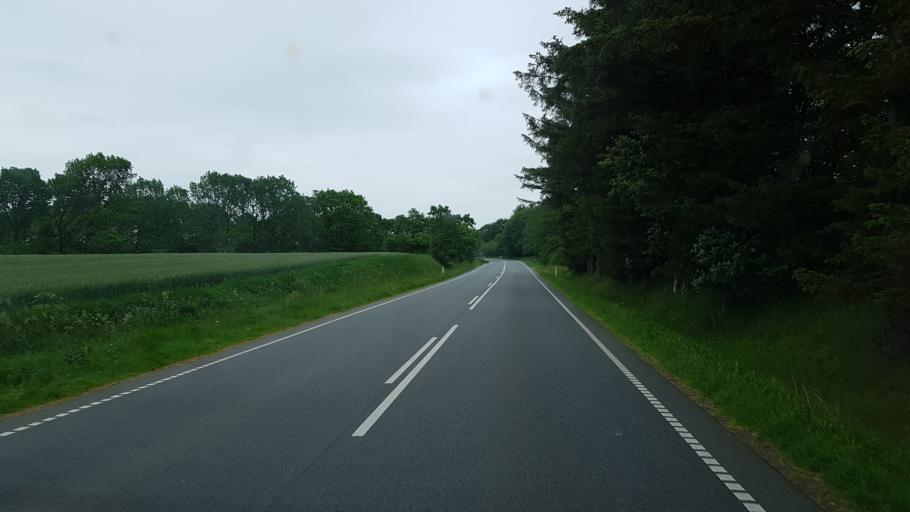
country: DK
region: South Denmark
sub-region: Varde Kommune
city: Olgod
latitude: 55.7221
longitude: 8.7184
